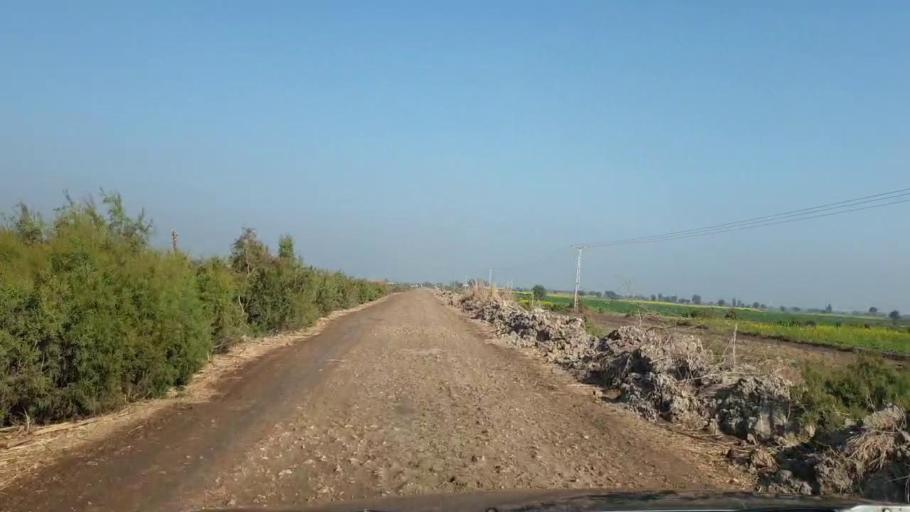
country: PK
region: Sindh
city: Sinjhoro
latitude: 26.0369
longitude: 68.7889
